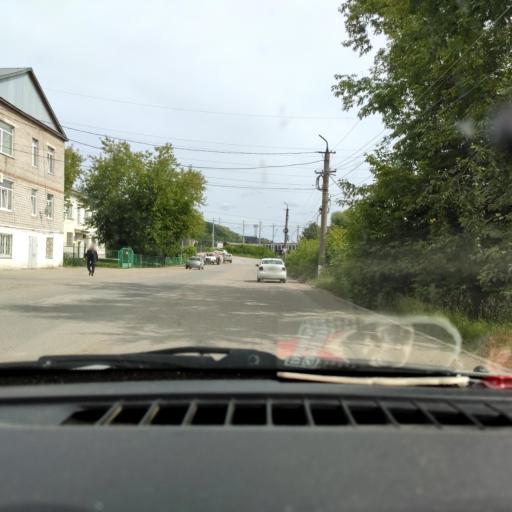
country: RU
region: Perm
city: Chusovoy
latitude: 58.2956
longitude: 57.8240
